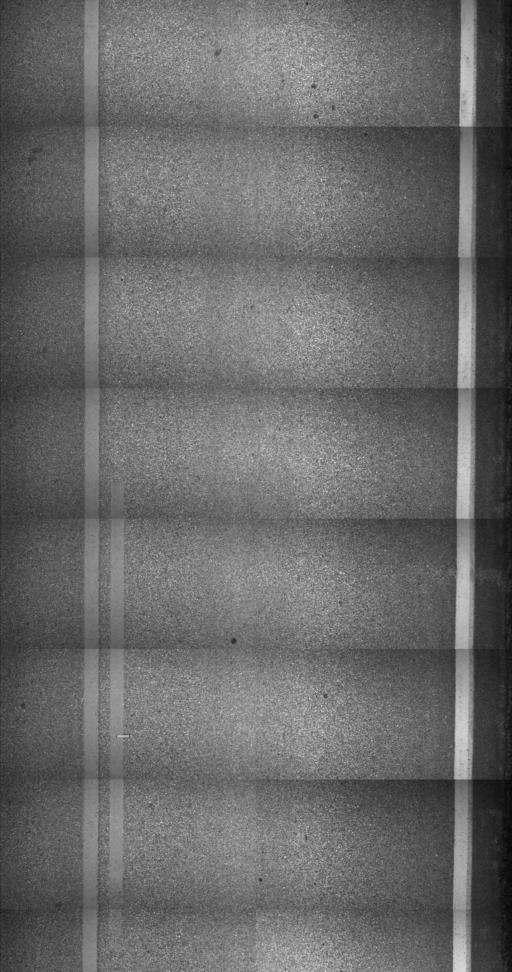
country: US
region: Vermont
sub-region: Rutland County
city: Poultney
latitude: 43.4818
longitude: -73.2416
